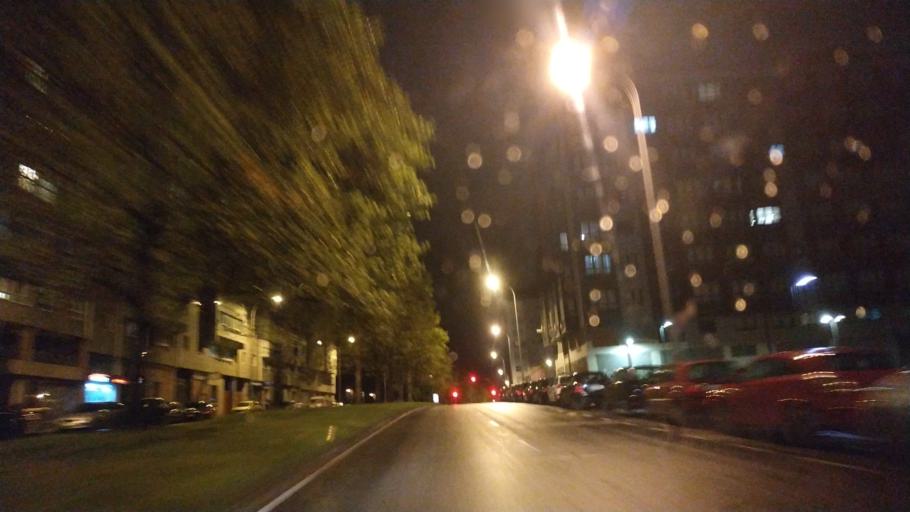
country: ES
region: Galicia
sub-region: Provincia da Coruna
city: A Coruna
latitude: 43.3536
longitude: -8.4149
